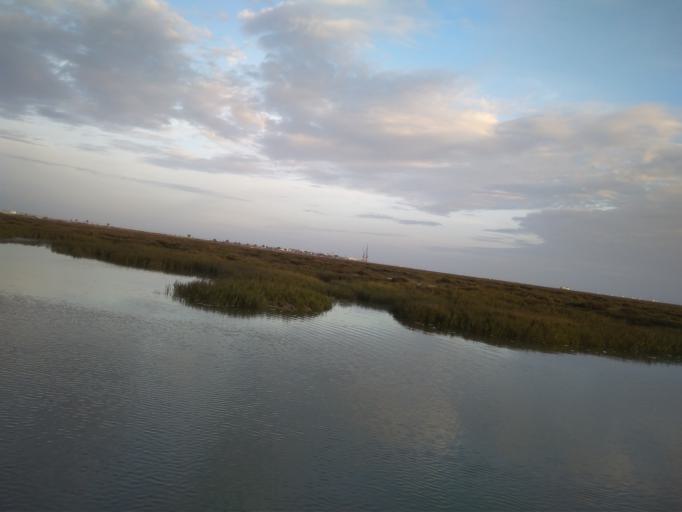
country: PT
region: Faro
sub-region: Faro
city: Faro
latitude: 37.0048
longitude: -7.9361
